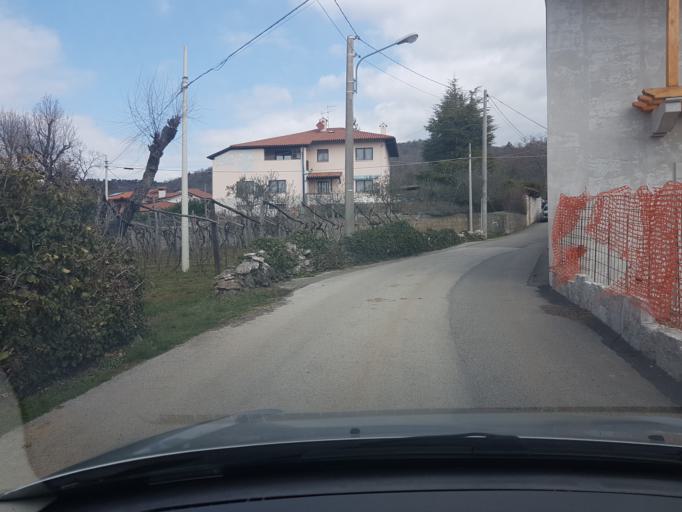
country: IT
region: Friuli Venezia Giulia
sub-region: Provincia di Trieste
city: Santa Croce
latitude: 45.7579
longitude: 13.7169
